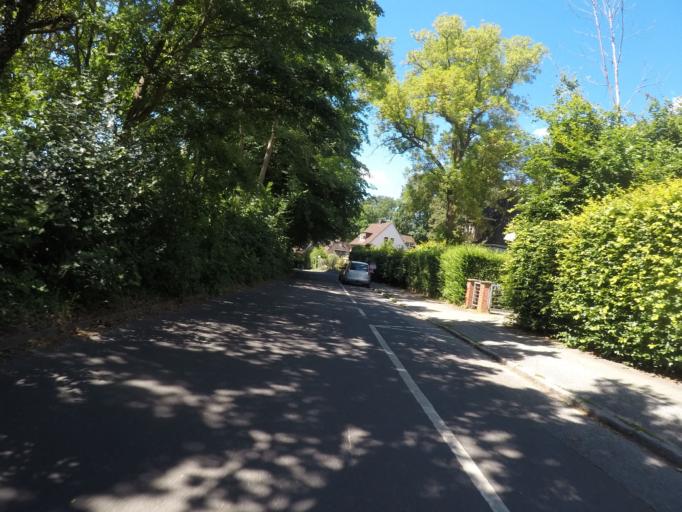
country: DE
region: Hamburg
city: Eidelstedt
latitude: 53.5584
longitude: 9.8740
